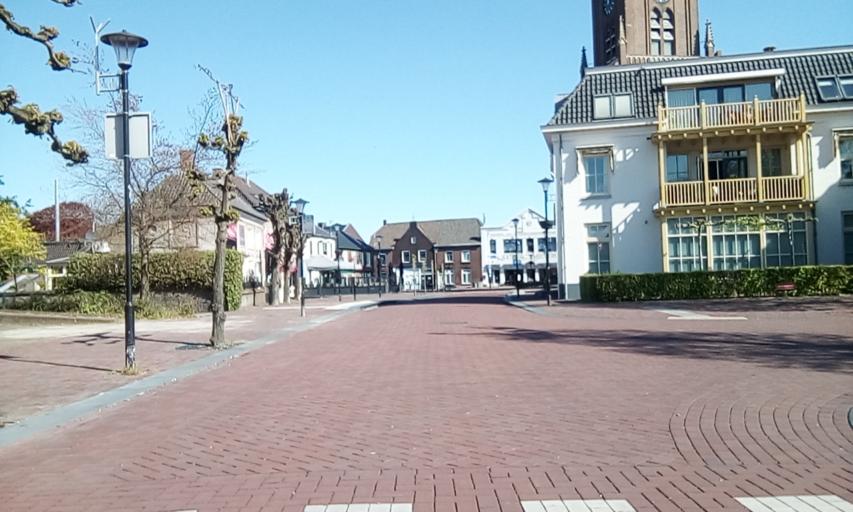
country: NL
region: Gelderland
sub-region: Gemeente Druten
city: Druten
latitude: 51.8907
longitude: 5.6089
